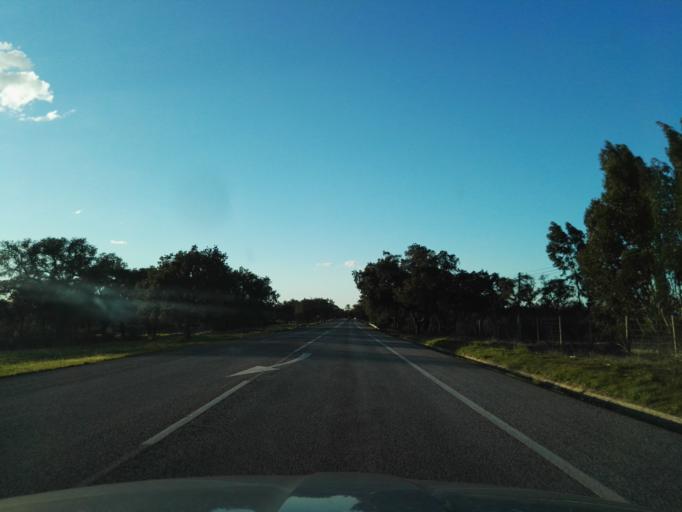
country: PT
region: Santarem
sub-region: Benavente
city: Poceirao
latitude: 38.8436
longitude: -8.7482
